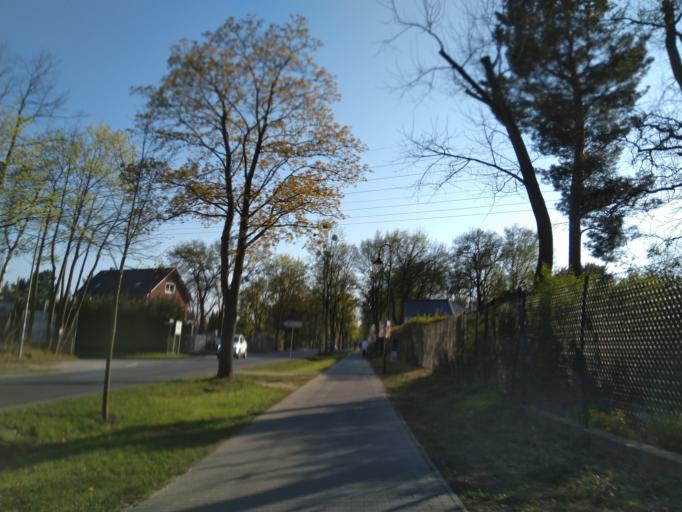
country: DE
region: Brandenburg
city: Bernau bei Berlin
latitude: 52.6713
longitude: 13.5633
